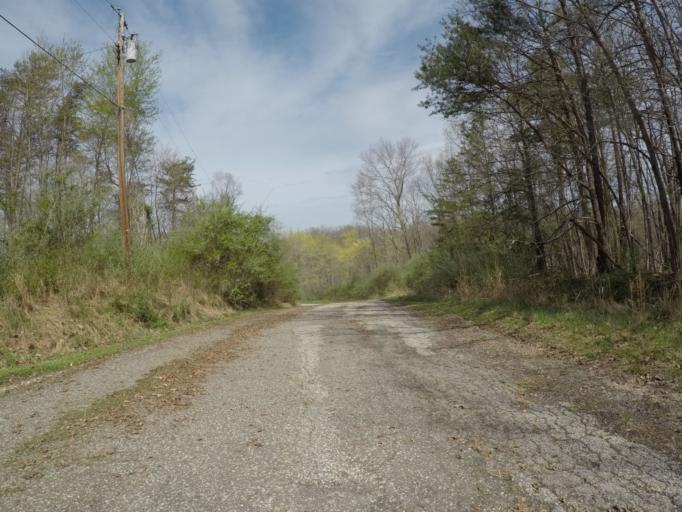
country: US
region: West Virginia
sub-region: Wayne County
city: Lavalette
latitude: 38.3307
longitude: -82.3602
